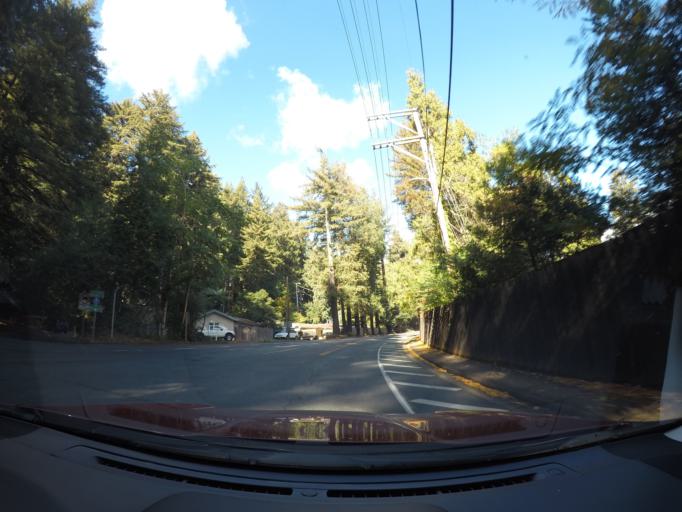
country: US
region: California
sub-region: Santa Cruz County
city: Ben Lomond
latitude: 37.0918
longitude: -122.0959
